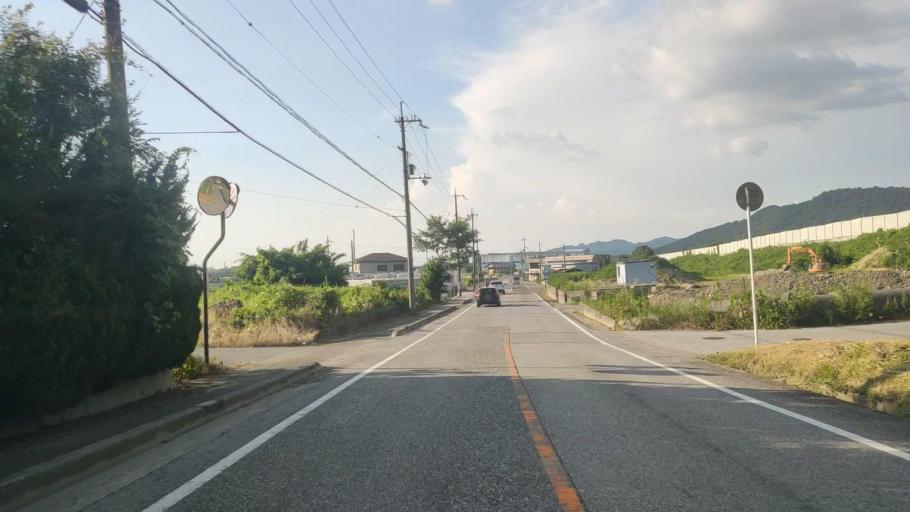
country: JP
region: Shiga Prefecture
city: Hikone
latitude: 35.1908
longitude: 136.2805
